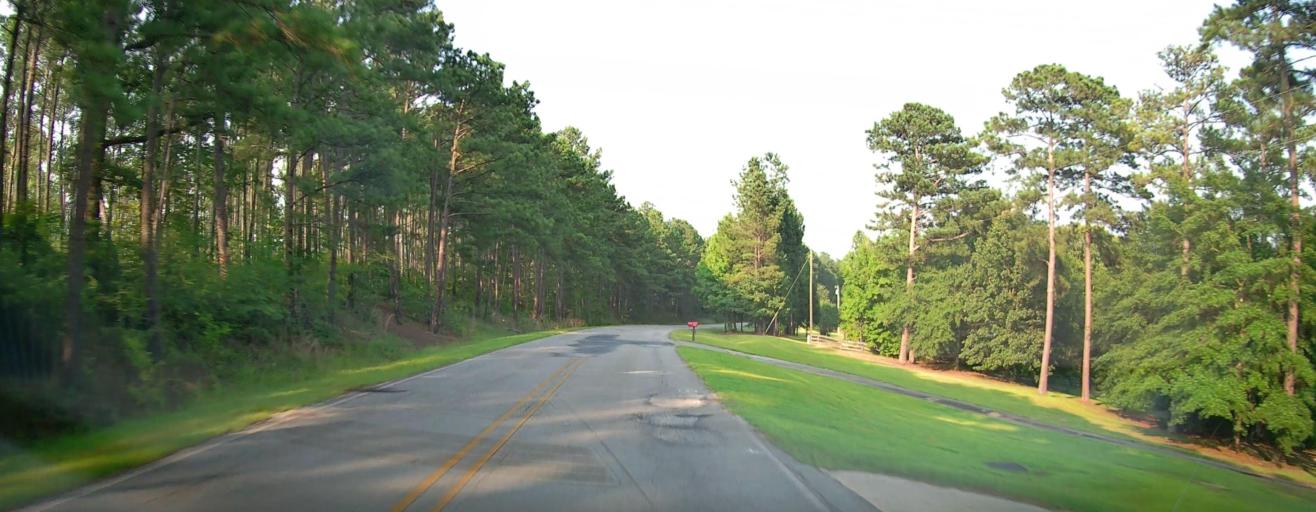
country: US
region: Georgia
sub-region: Monroe County
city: Forsyth
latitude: 33.0013
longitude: -83.7517
